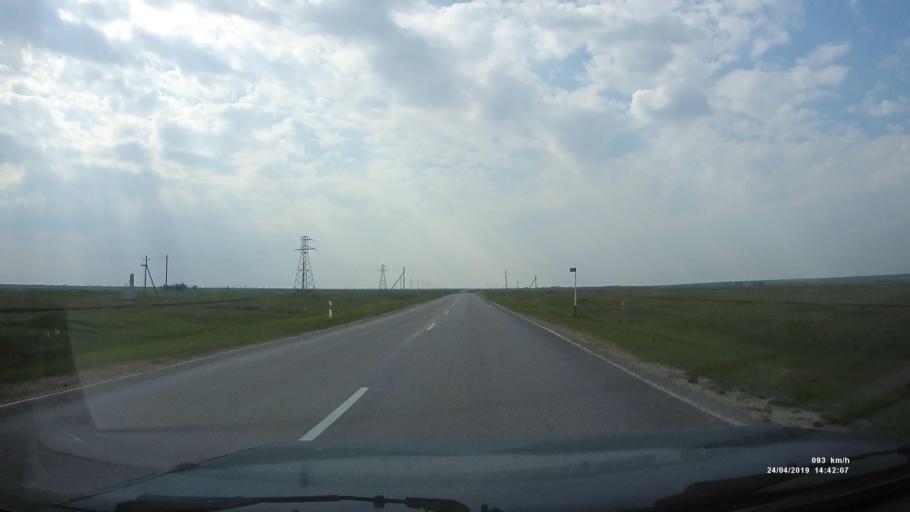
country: RU
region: Rostov
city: Remontnoye
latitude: 46.4504
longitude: 43.8685
